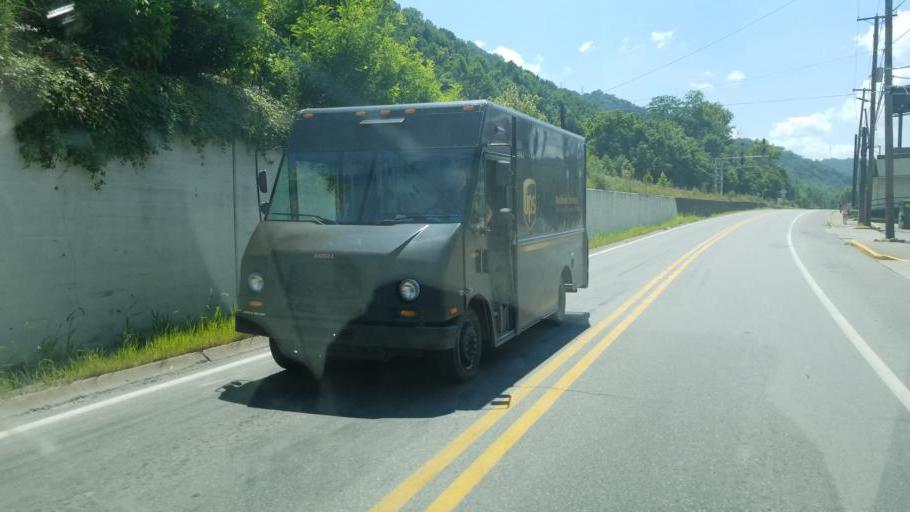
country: US
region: West Virginia
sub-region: Kanawha County
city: Chesapeake
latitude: 38.1962
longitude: -81.4808
